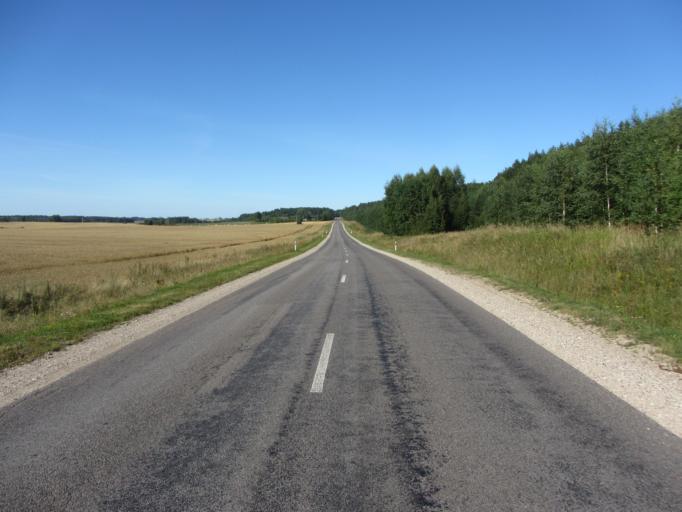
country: LT
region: Utenos apskritis
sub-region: Utena
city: Utena
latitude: 55.7276
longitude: 25.4327
